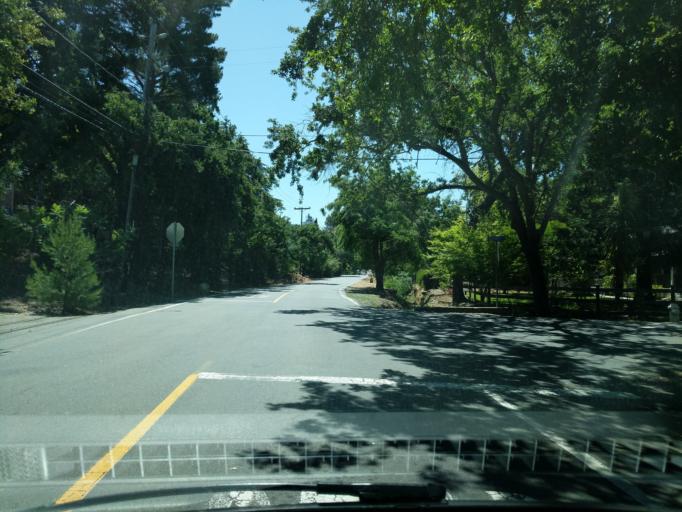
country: US
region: California
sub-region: Contra Costa County
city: Mountain View
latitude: 37.9889
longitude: -122.1228
